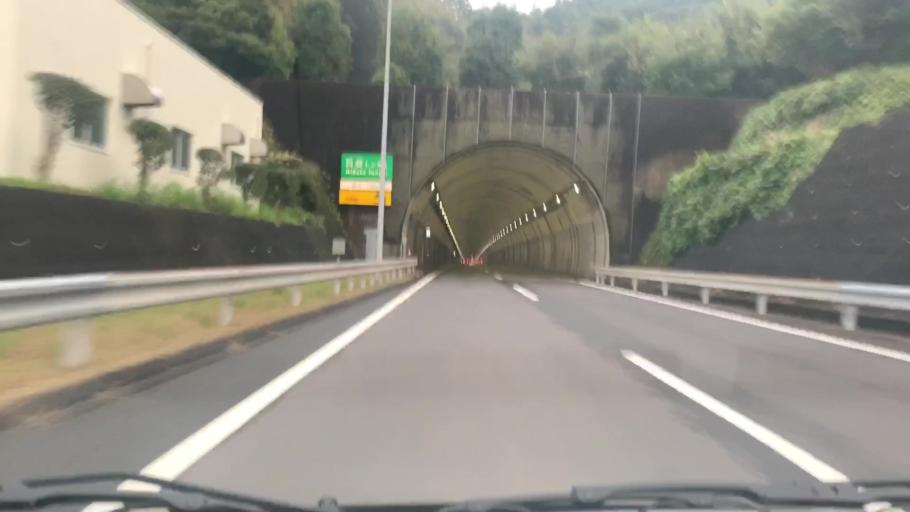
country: JP
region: Nagasaki
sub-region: Isahaya-shi
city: Isahaya
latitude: 32.8736
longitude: 129.9981
